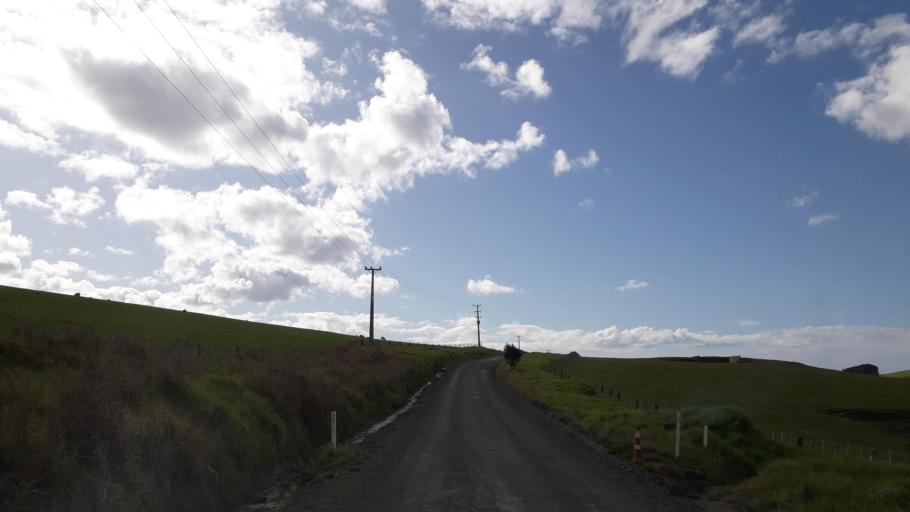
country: NZ
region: Northland
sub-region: Far North District
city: Kerikeri
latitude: -35.1472
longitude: 174.0379
